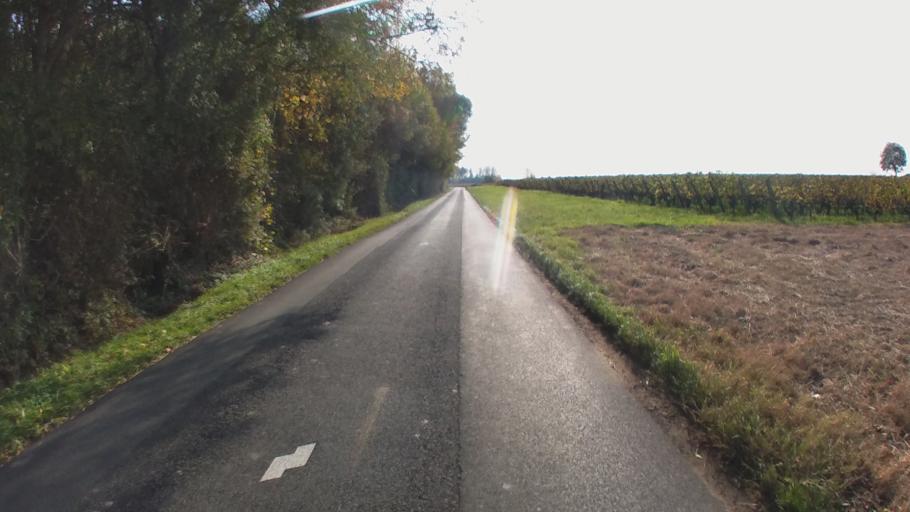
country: FR
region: Pays de la Loire
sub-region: Departement de Maine-et-Loire
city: Chace
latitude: 47.2145
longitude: -0.0906
